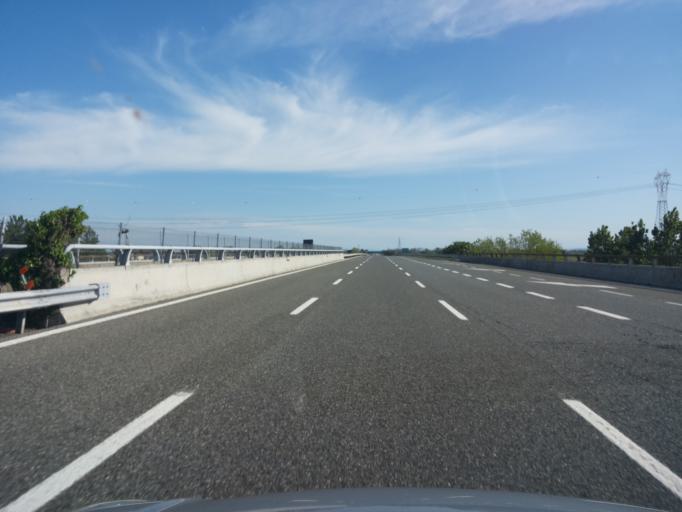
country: IT
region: Piedmont
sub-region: Provincia di Novara
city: Biandrate
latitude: 45.4576
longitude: 8.4531
